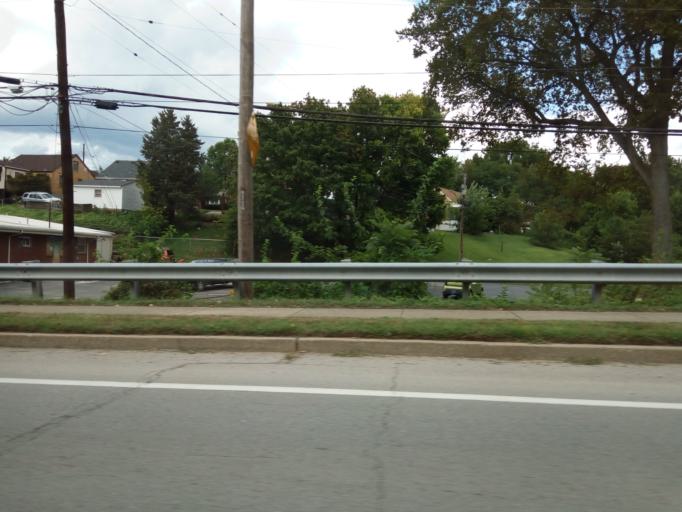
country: US
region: Kentucky
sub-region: Jefferson County
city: Audubon Park
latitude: 38.2072
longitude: -85.7145
